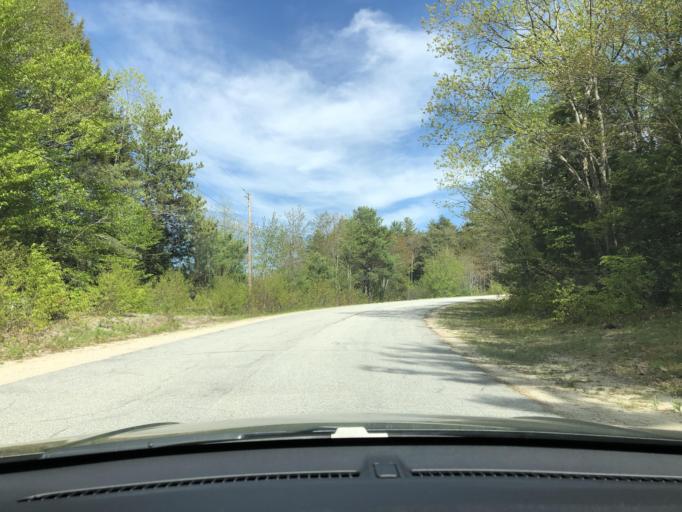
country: US
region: New Hampshire
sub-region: Merrimack County
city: New London
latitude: 43.4101
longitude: -72.0304
